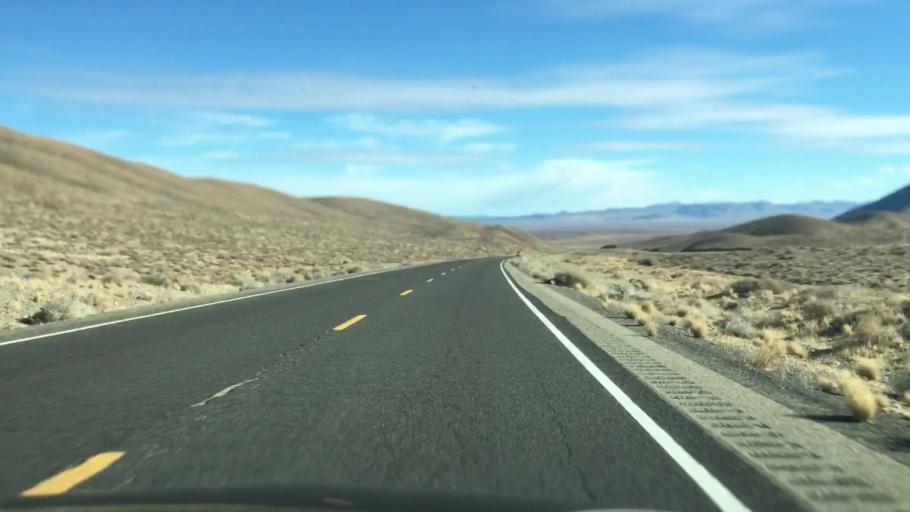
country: US
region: Nevada
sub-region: Lyon County
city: Yerington
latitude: 39.0398
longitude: -118.9392
